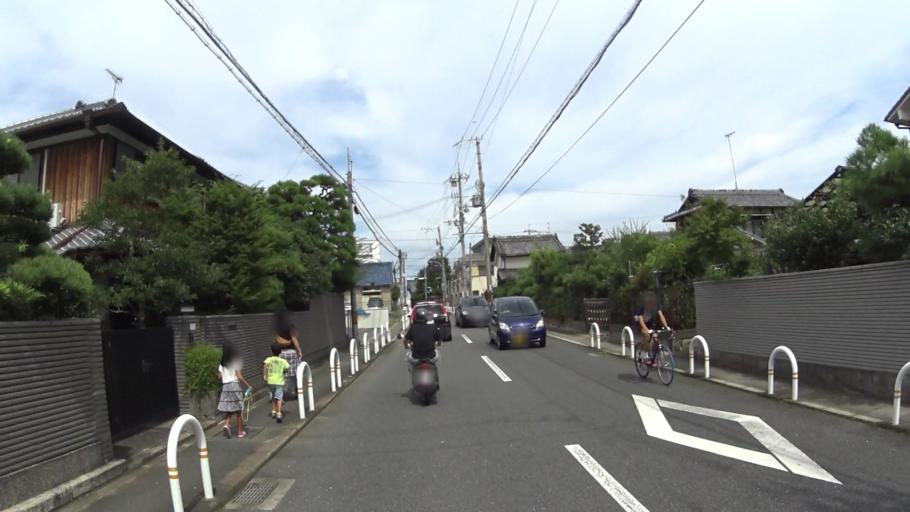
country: JP
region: Kyoto
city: Muko
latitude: 34.9509
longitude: 135.6990
